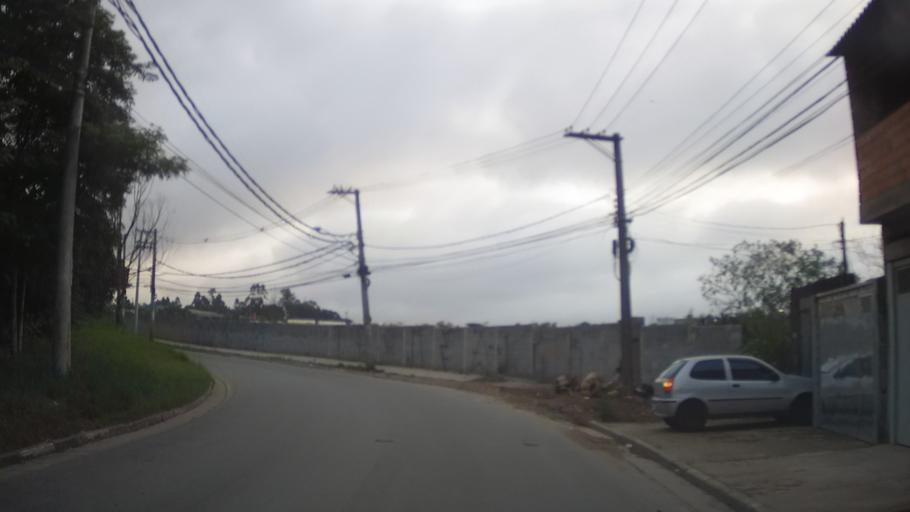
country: BR
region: Sao Paulo
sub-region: Itaquaquecetuba
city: Itaquaquecetuba
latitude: -23.4639
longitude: -46.4370
